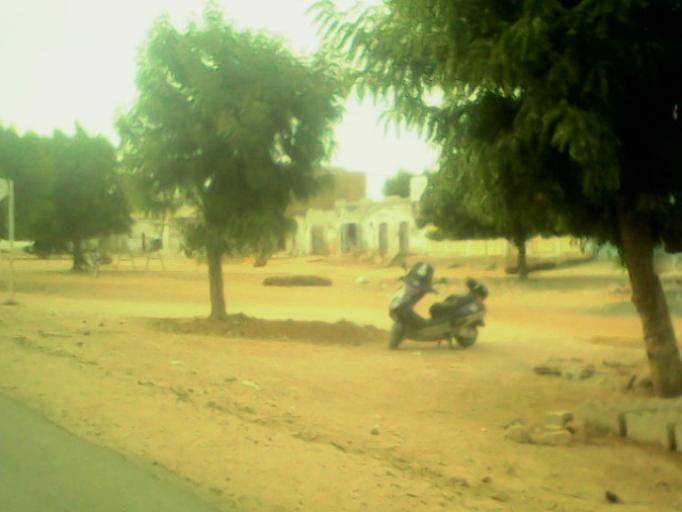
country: SN
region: Diourbel
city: Touba
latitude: 14.8833
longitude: -15.8830
